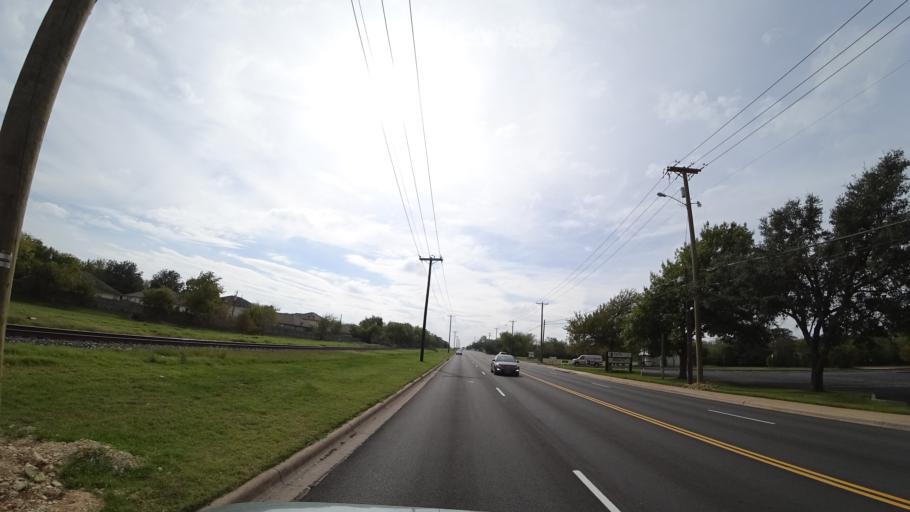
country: US
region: Texas
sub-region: Williamson County
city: Round Rock
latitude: 30.4944
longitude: -97.6915
